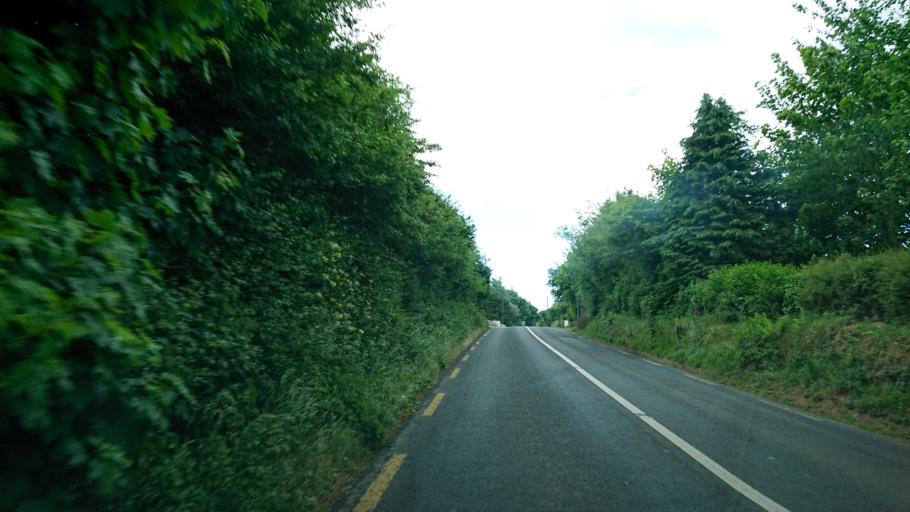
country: IE
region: Munster
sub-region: Waterford
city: Tra Mhor
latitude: 52.1823
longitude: -7.1722
